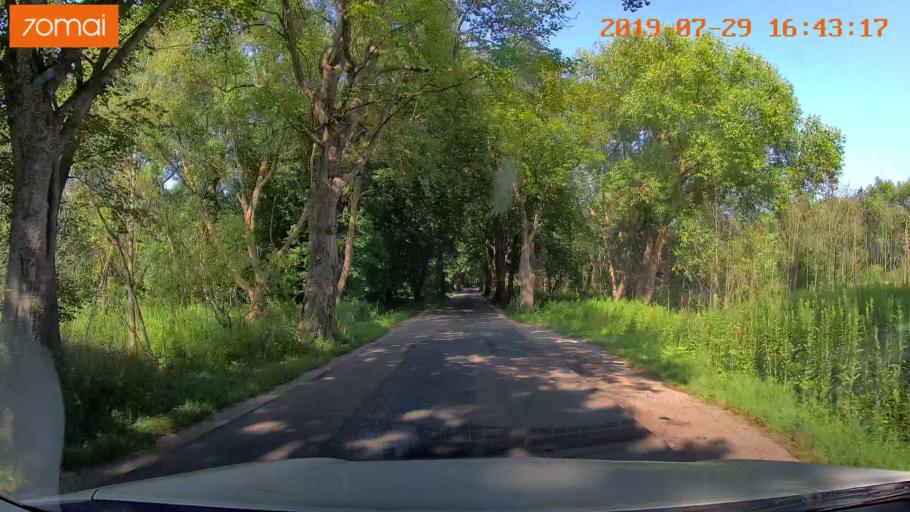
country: RU
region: Kaliningrad
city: Primorsk
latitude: 54.7480
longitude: 20.0826
